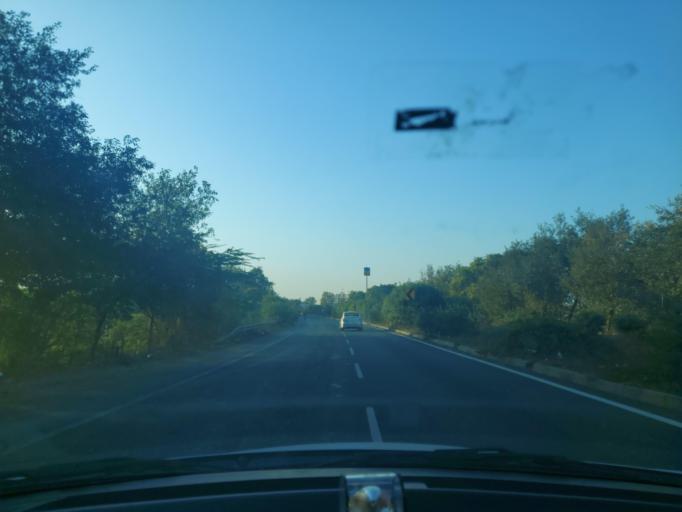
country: IN
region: Madhya Pradesh
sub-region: Ujjain
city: Ujjain
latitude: 23.0966
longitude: 75.8147
